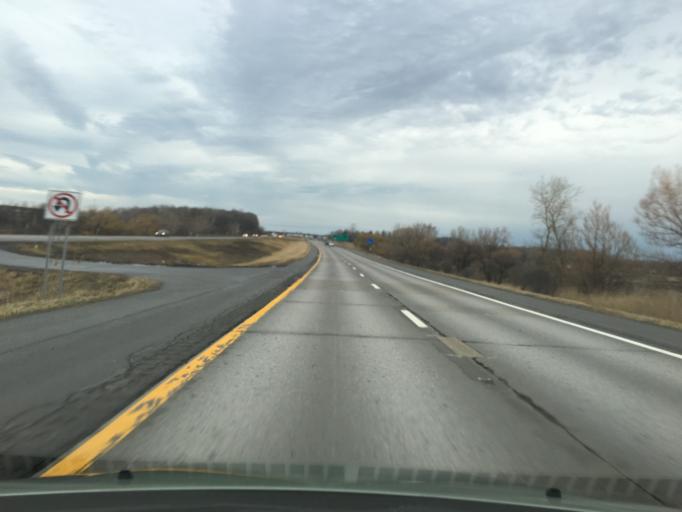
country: US
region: New York
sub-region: Monroe County
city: Scottsville
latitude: 43.0438
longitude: -77.6494
